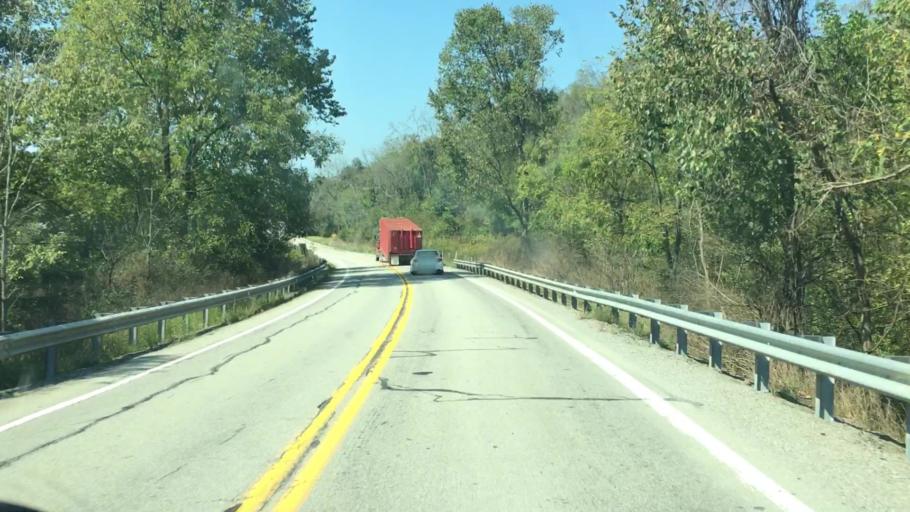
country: US
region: Pennsylvania
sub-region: Washington County
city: Washington
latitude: 40.0416
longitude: -80.2818
